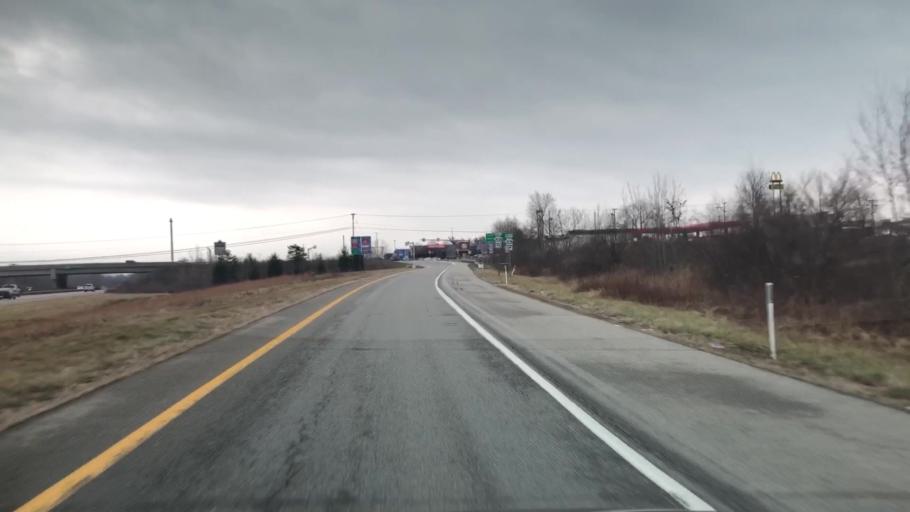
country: US
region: Pennsylvania
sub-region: Mercer County
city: Grove City
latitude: 41.1460
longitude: -80.1560
